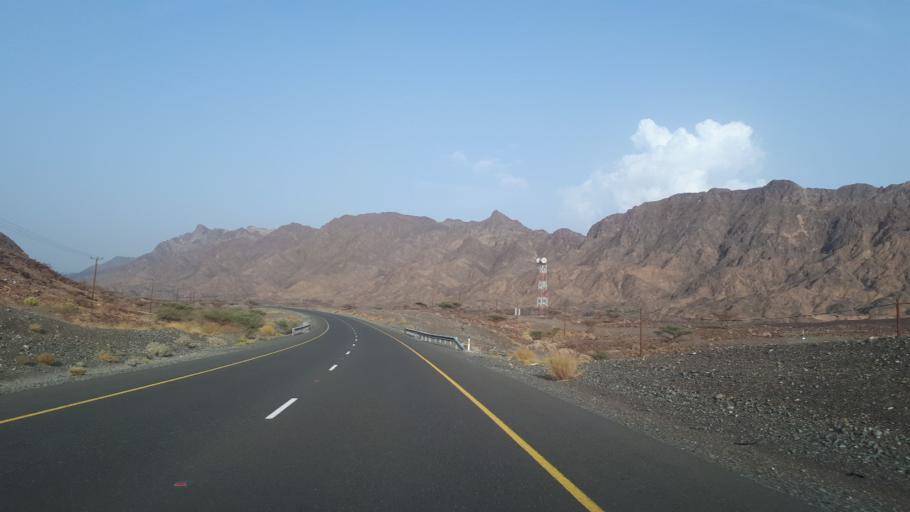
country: OM
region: Az Zahirah
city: Yanqul
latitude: 23.4926
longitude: 56.8661
